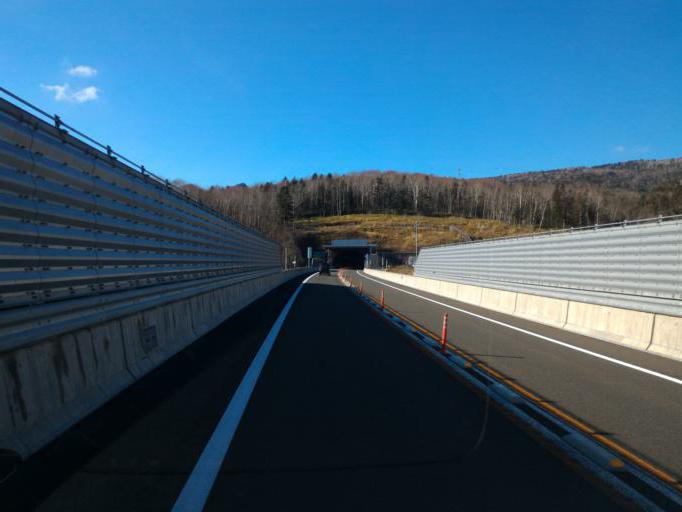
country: JP
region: Hokkaido
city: Shimo-furano
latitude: 42.9512
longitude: 142.3096
